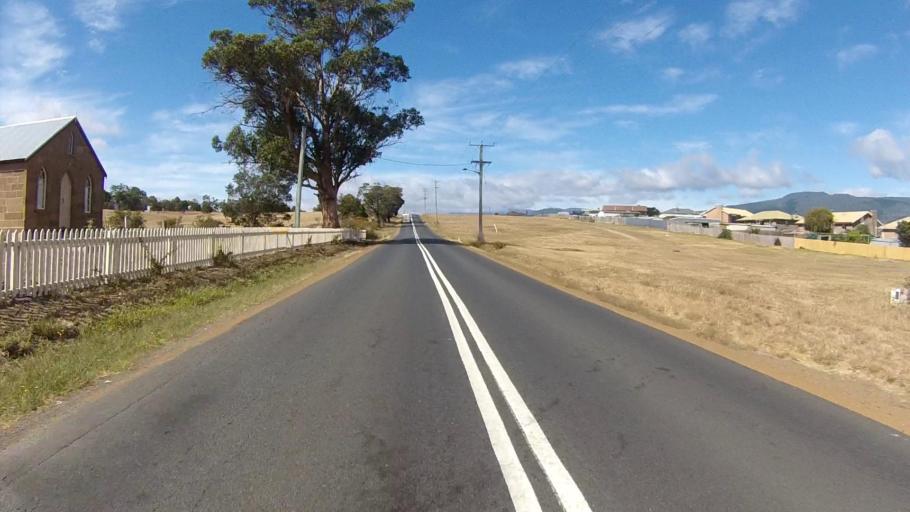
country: AU
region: Tasmania
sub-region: Brighton
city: Old Beach
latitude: -42.7464
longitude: 147.2811
